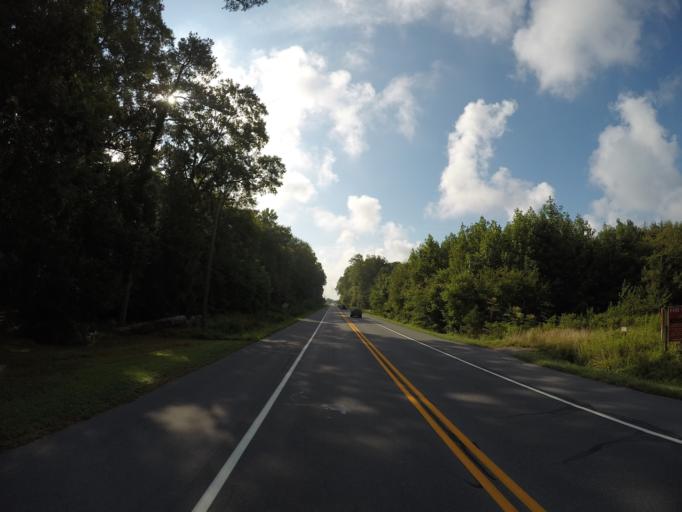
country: US
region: Delaware
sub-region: Sussex County
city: Bridgeville
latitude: 38.7631
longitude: -75.6419
